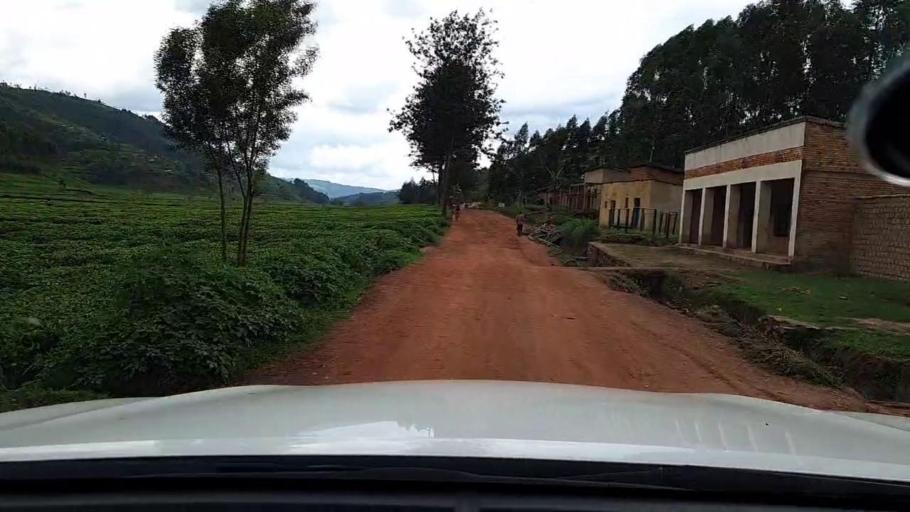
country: RW
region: Northern Province
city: Byumba
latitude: -1.6686
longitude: 29.9237
